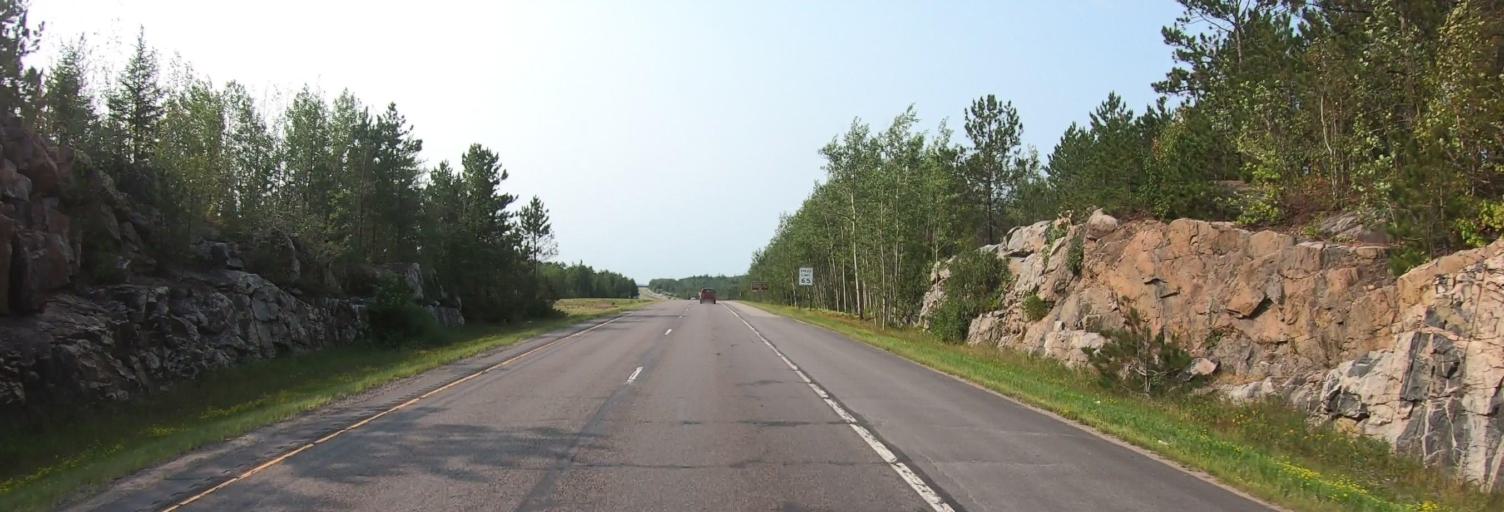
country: US
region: Minnesota
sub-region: Saint Louis County
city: Virginia
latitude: 47.5783
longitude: -92.5445
